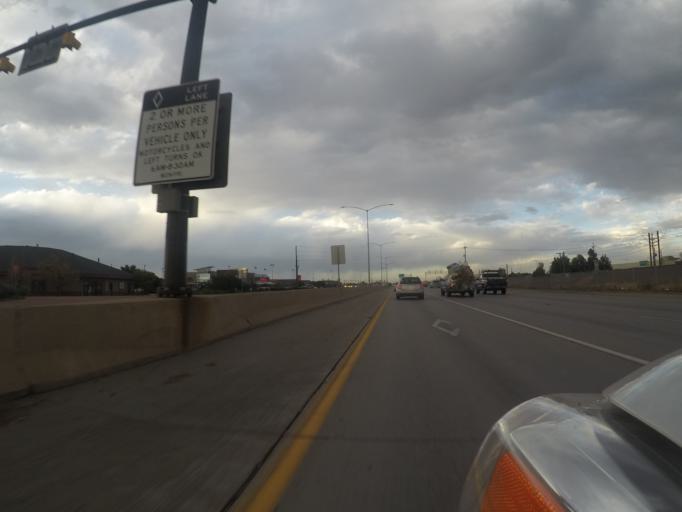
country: US
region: Colorado
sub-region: Arapahoe County
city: Englewood
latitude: 39.6484
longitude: -105.0034
